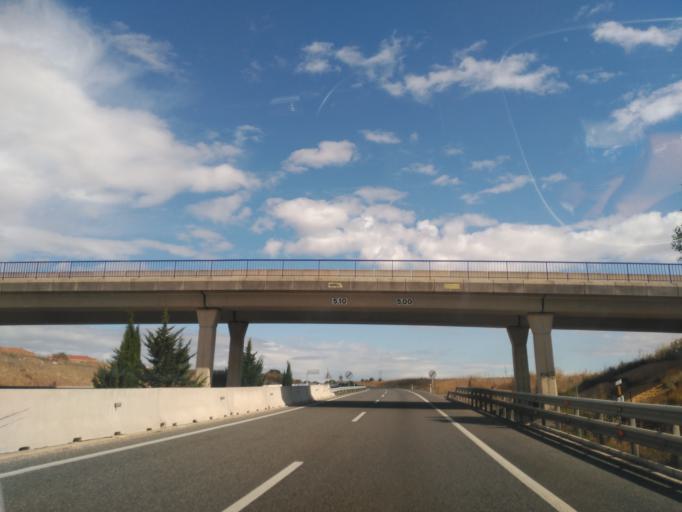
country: ES
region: Castille and Leon
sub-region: Provincia de Burgos
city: Buniel
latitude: 42.3101
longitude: -3.8131
